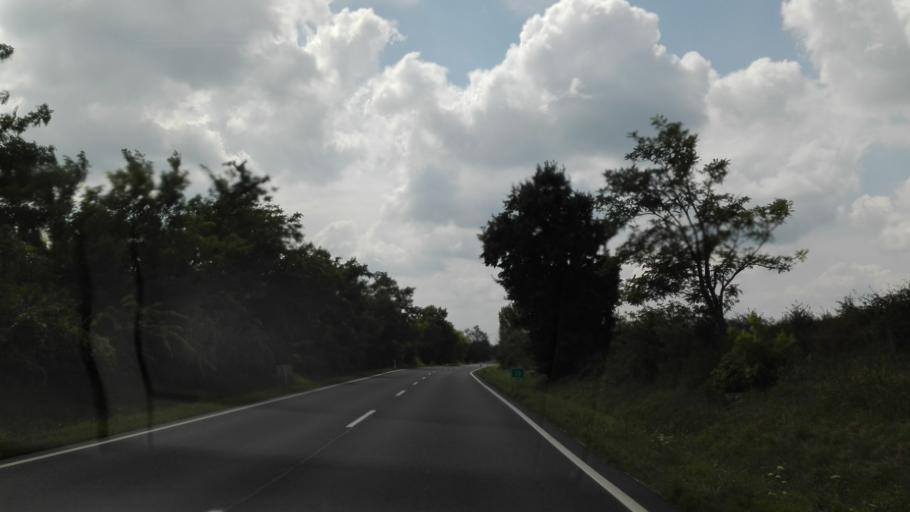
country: HU
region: Fejer
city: Alap
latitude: 46.8047
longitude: 18.7620
